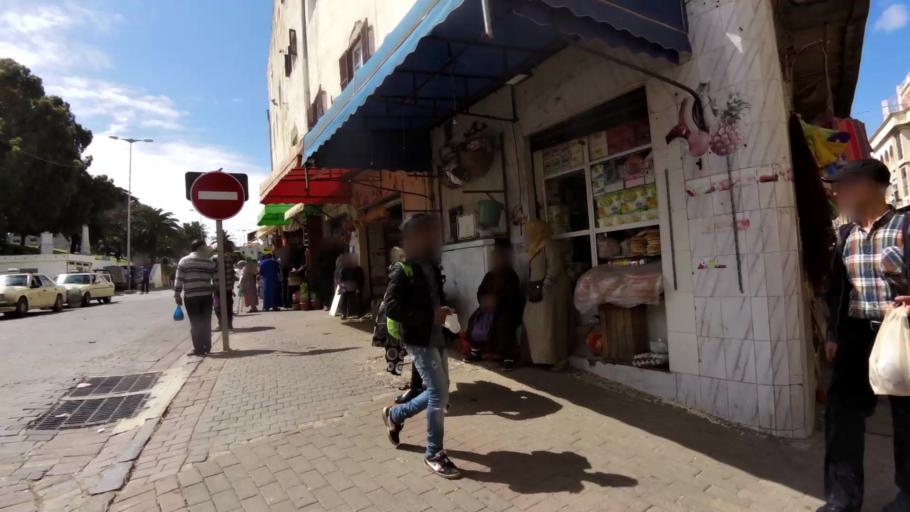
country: MA
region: Tanger-Tetouan
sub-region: Tanger-Assilah
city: Tangier
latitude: 35.7860
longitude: -5.8131
